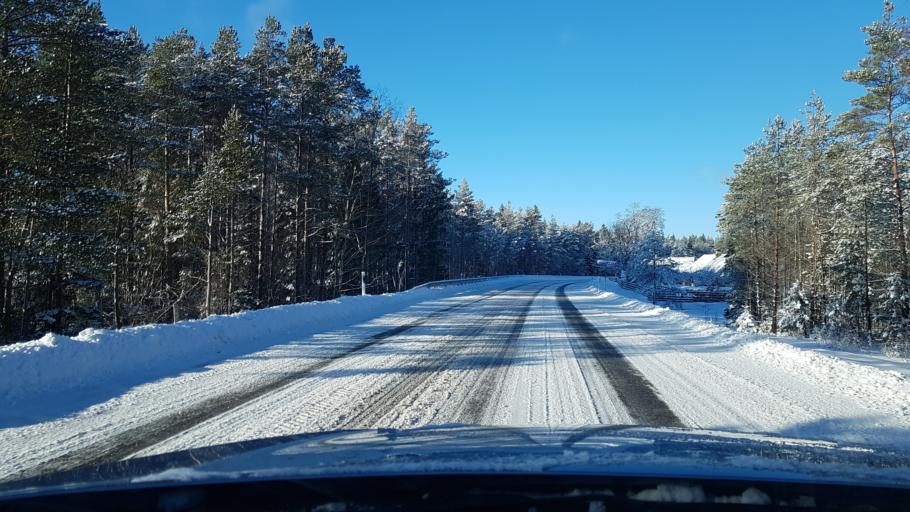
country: EE
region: Hiiumaa
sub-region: Kaerdla linn
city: Kardla
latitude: 58.9734
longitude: 22.7652
